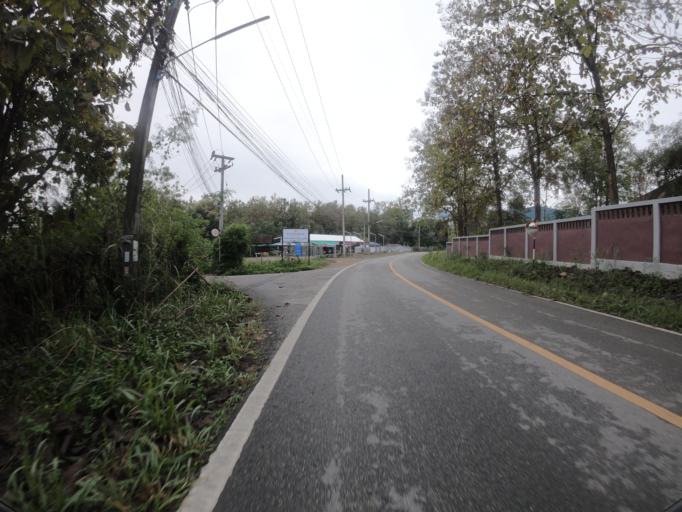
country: TH
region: Chiang Mai
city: Hang Dong
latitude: 18.7407
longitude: 98.9243
